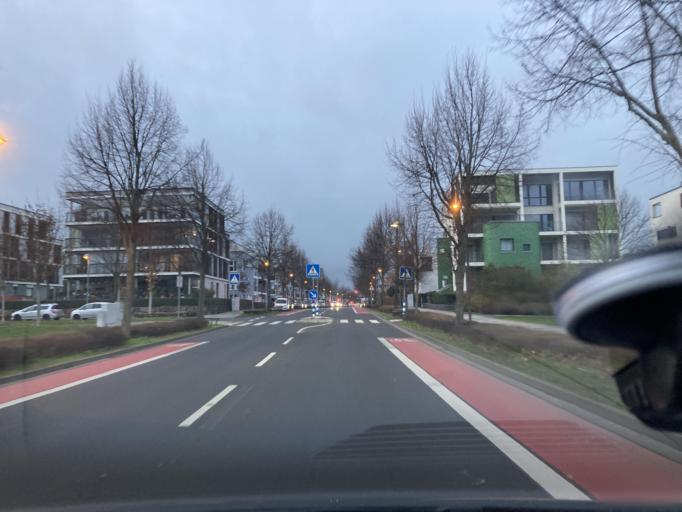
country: DE
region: Hesse
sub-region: Regierungsbezirk Darmstadt
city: Bad Homburg vor der Hoehe
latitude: 50.1800
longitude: 8.6273
